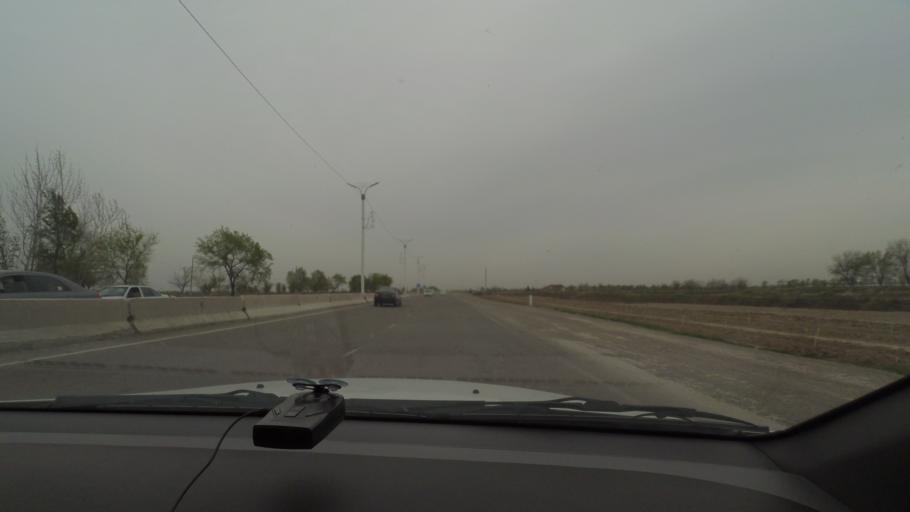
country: KZ
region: Ongtustik Qazaqstan
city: Myrzakent
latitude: 40.5377
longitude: 68.4258
